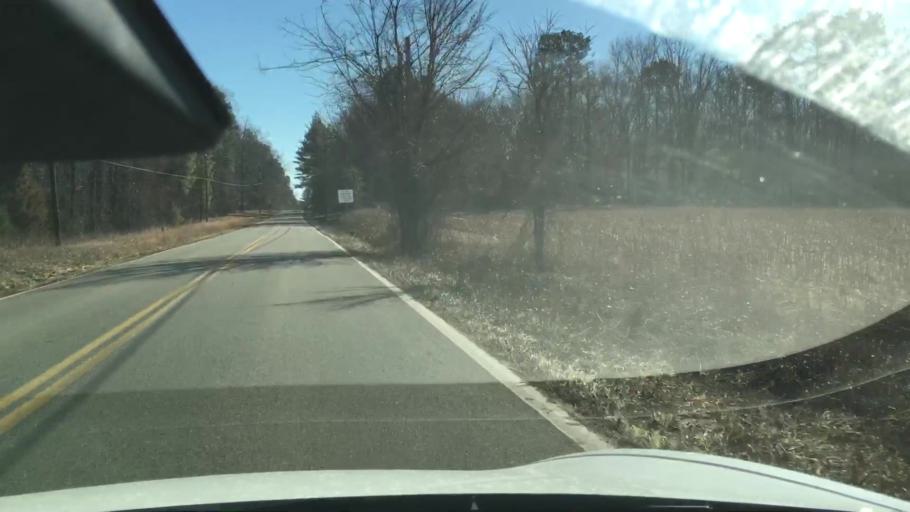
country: US
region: Virginia
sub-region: Henrico County
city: Short Pump
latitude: 37.5751
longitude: -77.7214
